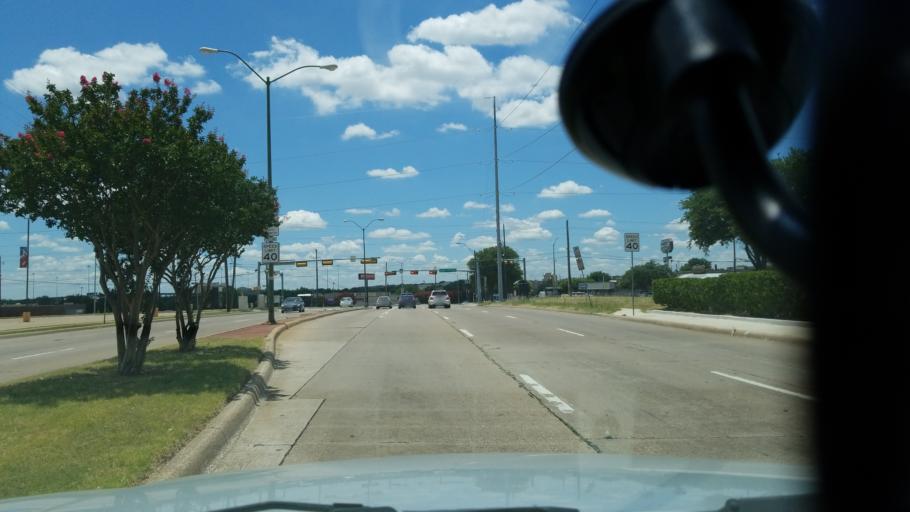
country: US
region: Texas
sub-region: Dallas County
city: Duncanville
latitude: 32.6630
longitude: -96.8817
